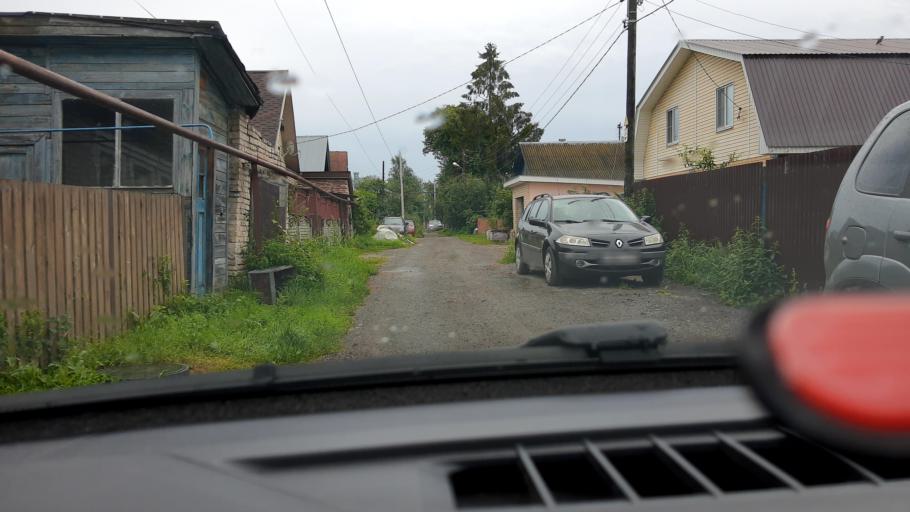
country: RU
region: Nizjnij Novgorod
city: Gorbatovka
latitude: 56.3749
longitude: 43.8268
